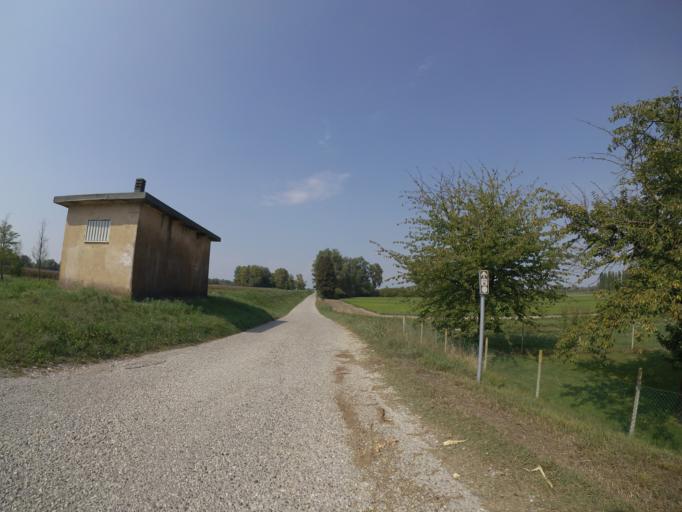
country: IT
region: Friuli Venezia Giulia
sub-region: Provincia di Udine
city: Camino al Tagliamento
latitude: 45.9013
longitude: 12.9389
